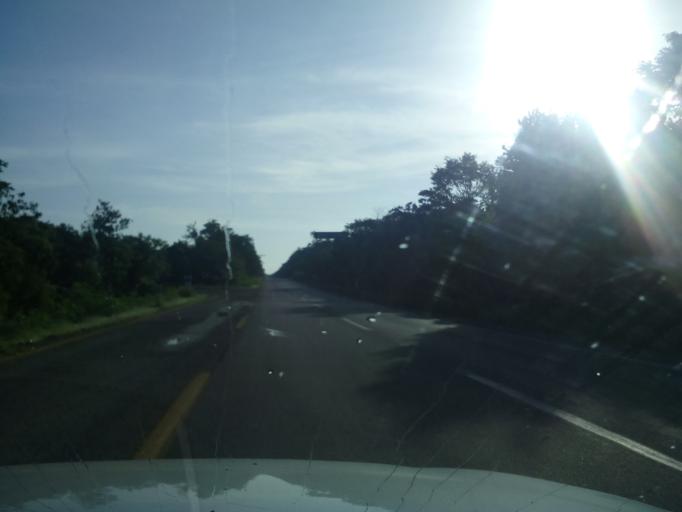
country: MX
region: Yucatan
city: Tinum
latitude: 20.7164
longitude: -88.4083
